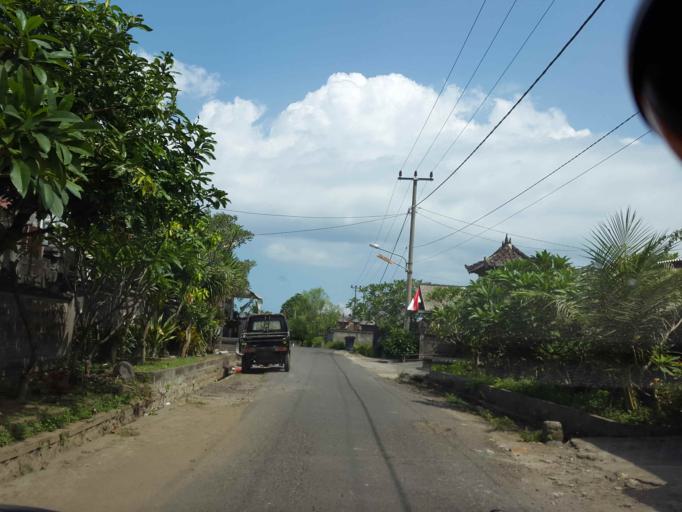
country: ID
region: Bali
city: Klungkung
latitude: -8.5527
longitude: 115.3785
